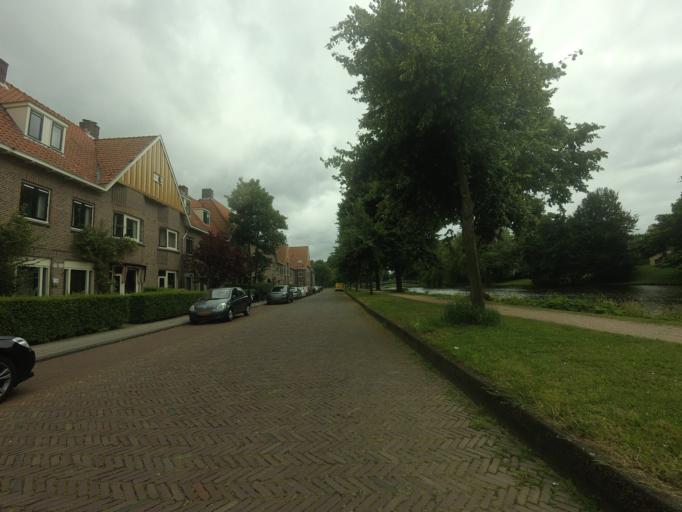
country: NL
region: North Holland
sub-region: Gemeente Haarlem
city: Haarlem
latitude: 52.3894
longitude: 4.6441
